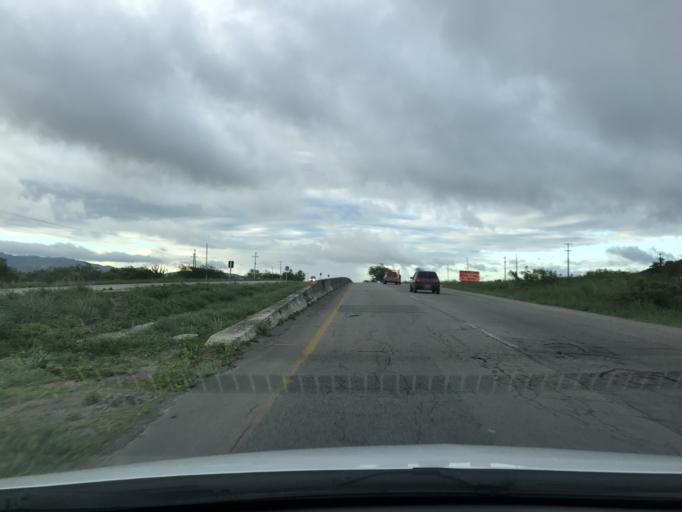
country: BR
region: Pernambuco
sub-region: Bezerros
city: Bezerros
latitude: -8.2866
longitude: -35.8176
